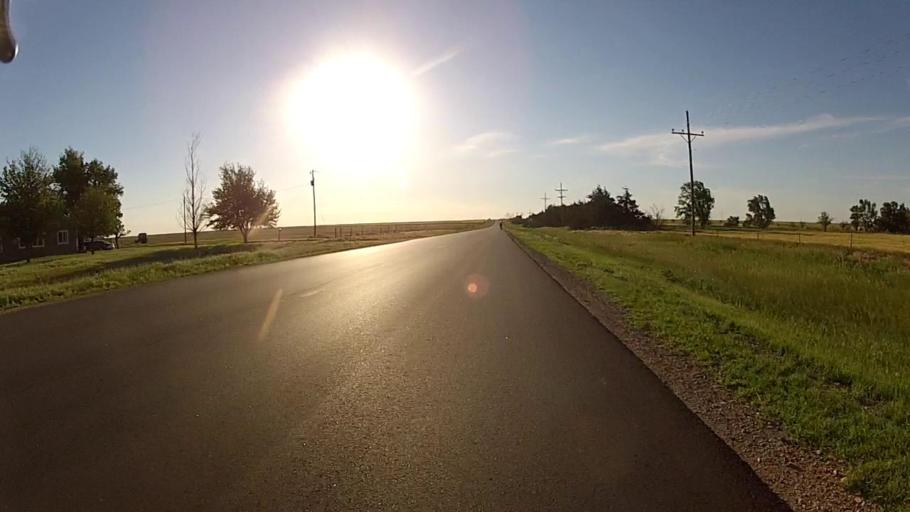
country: US
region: Kansas
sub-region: Comanche County
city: Coldwater
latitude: 37.2816
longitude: -99.1735
